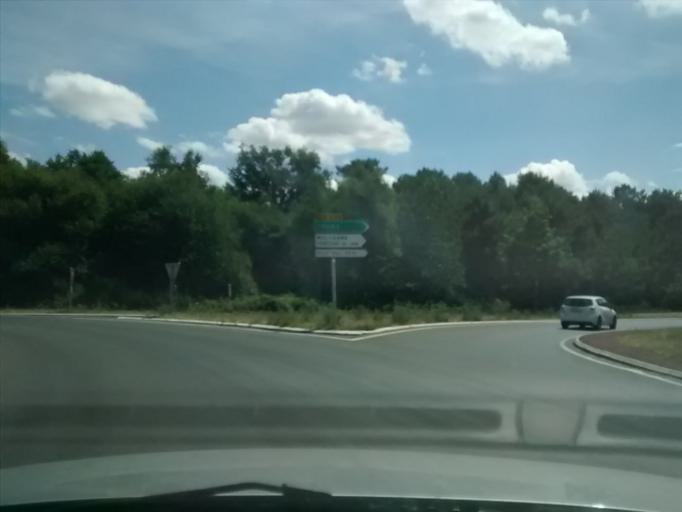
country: FR
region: Pays de la Loire
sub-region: Departement de la Sarthe
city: Ruaudin
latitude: 47.9410
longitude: 0.2357
